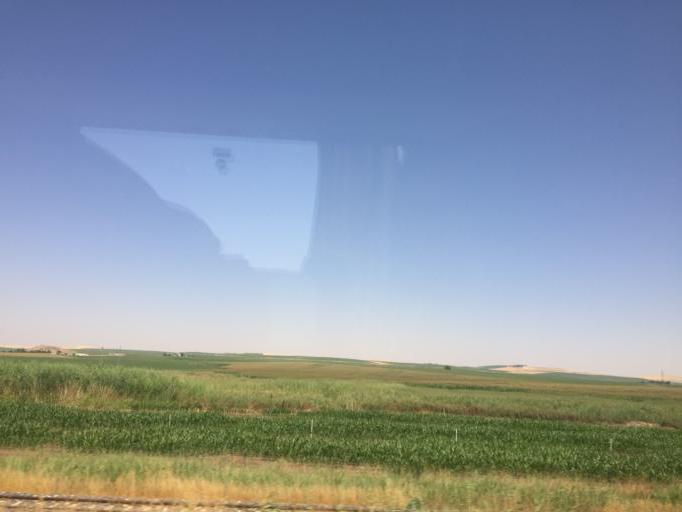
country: TR
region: Diyarbakir
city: Tepe
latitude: 37.8511
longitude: 40.7626
